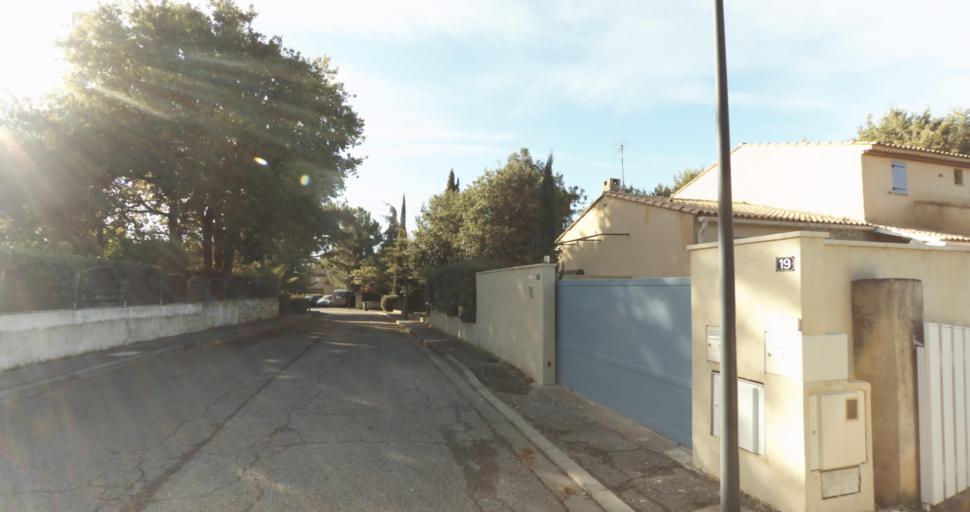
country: FR
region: Provence-Alpes-Cote d'Azur
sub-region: Departement des Bouches-du-Rhone
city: Venelles
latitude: 43.5914
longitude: 5.4659
